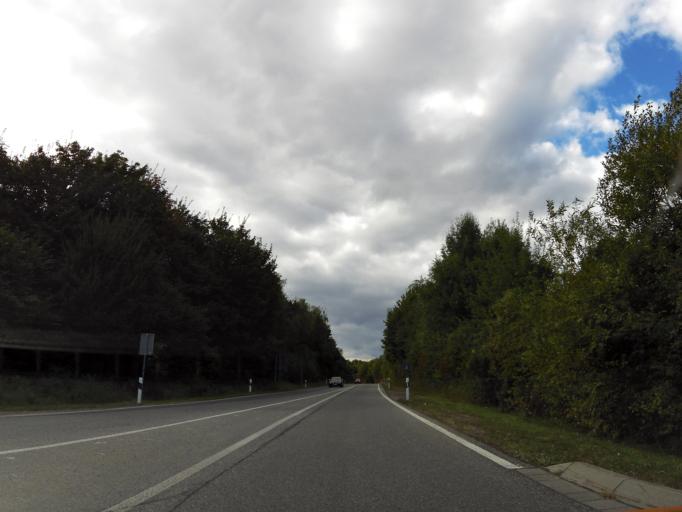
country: DE
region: Rheinland-Pfalz
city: Klein-Winternheim
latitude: 49.9495
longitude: 8.2192
